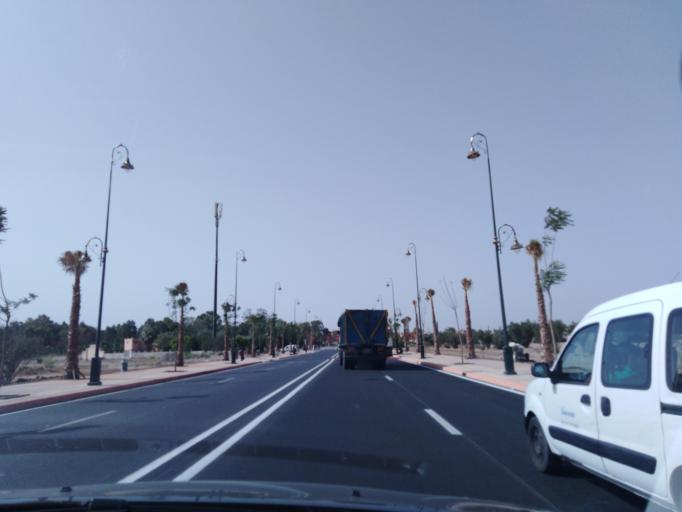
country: MA
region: Marrakech-Tensift-Al Haouz
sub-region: Kelaa-Des-Sraghna
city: Sidi Bou Othmane
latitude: 32.2270
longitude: -7.9570
